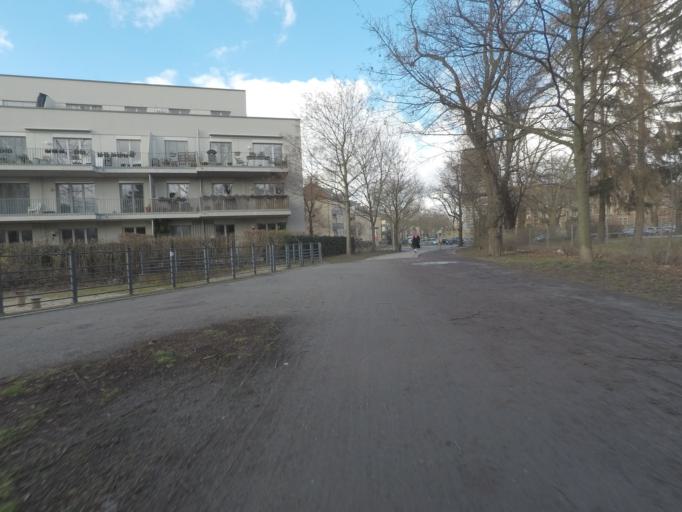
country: DE
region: Berlin
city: Britz
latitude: 52.4620
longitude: 13.4221
